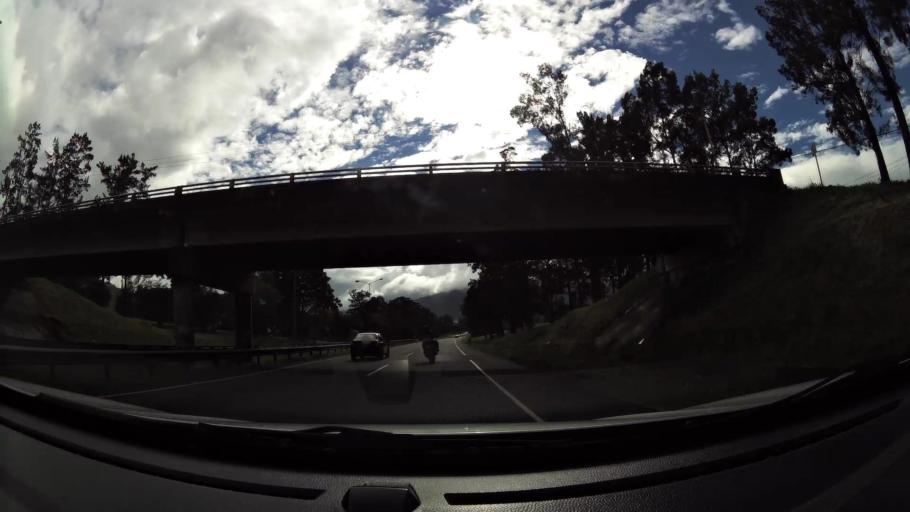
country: CR
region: San Jose
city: Curridabat
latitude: 9.9096
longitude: -84.0176
